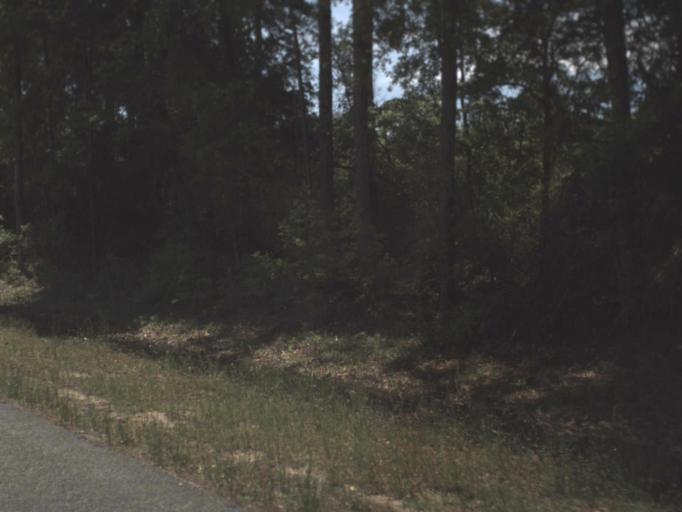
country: US
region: Florida
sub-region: Jackson County
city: Marianna
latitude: 30.6344
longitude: -85.1892
